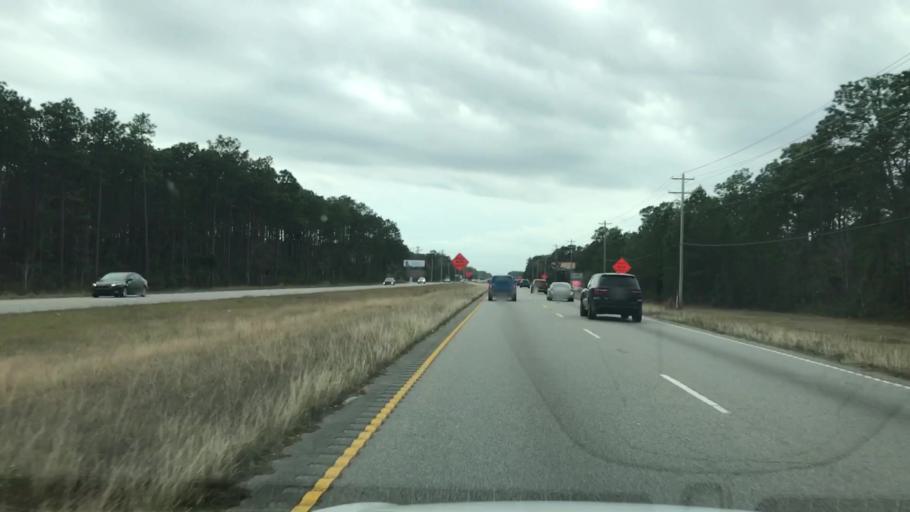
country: US
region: South Carolina
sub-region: Horry County
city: Surfside Beach
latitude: 33.6339
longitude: -78.9941
